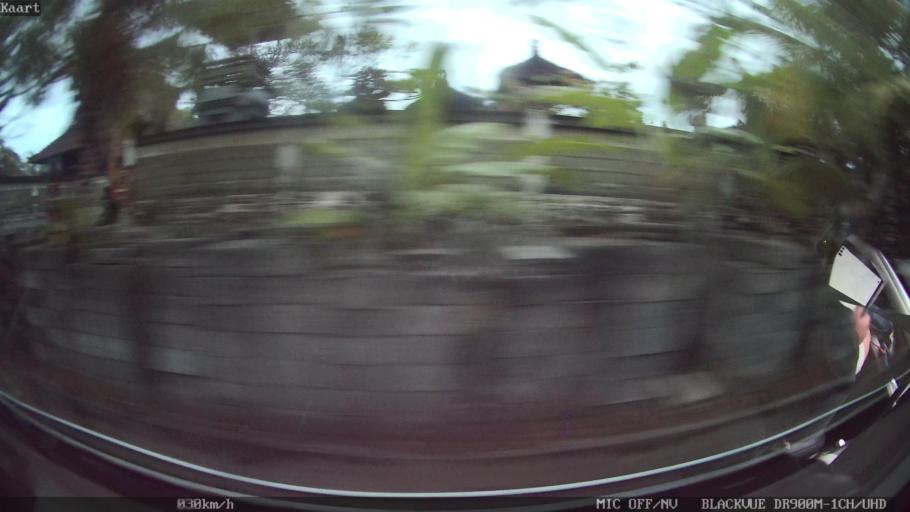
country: ID
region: Bali
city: Banjar Pasekan
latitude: -8.6121
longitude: 115.2863
